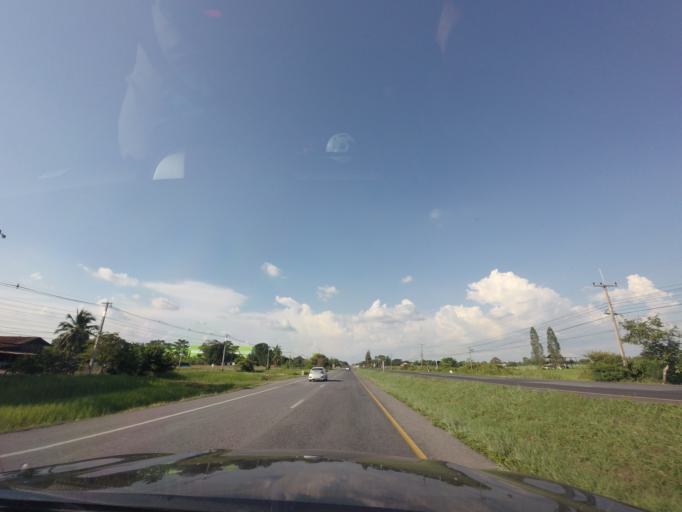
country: TH
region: Khon Kaen
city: Non Sila
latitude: 16.0022
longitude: 102.7023
